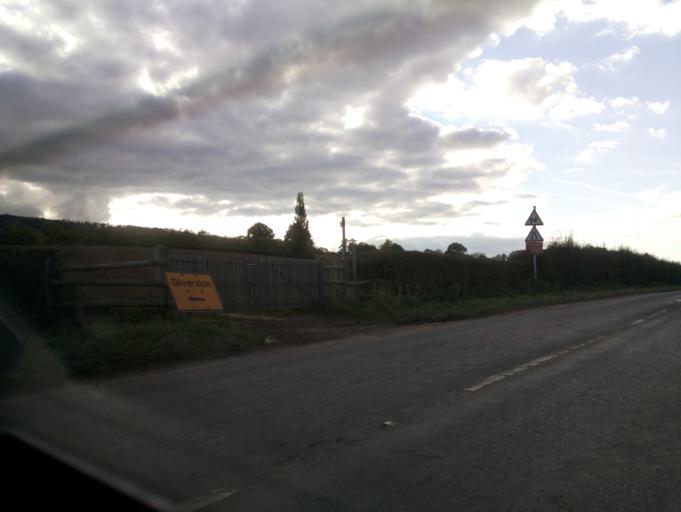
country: GB
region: England
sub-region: Herefordshire
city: Ocle Pychard
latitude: 52.0646
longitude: -2.5506
